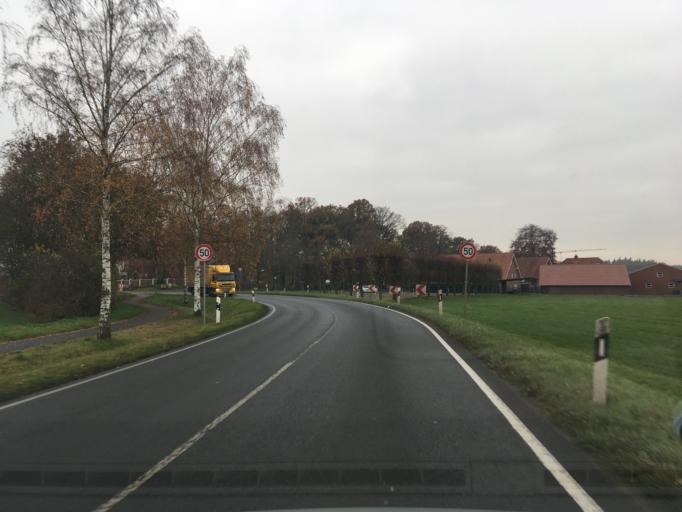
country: DE
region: North Rhine-Westphalia
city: Stadtlohn
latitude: 51.9858
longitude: 6.9459
